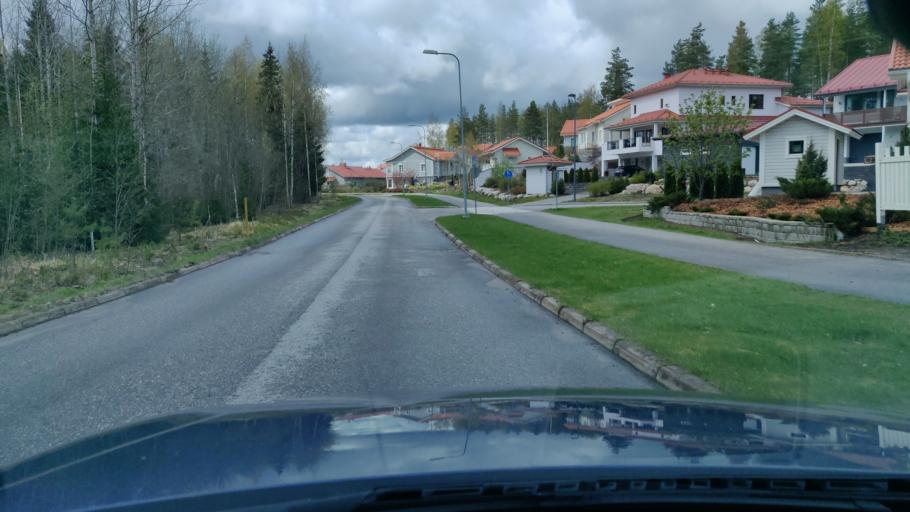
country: FI
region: Uusimaa
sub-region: Helsinki
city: Nurmijaervi
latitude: 60.3636
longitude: 24.7313
